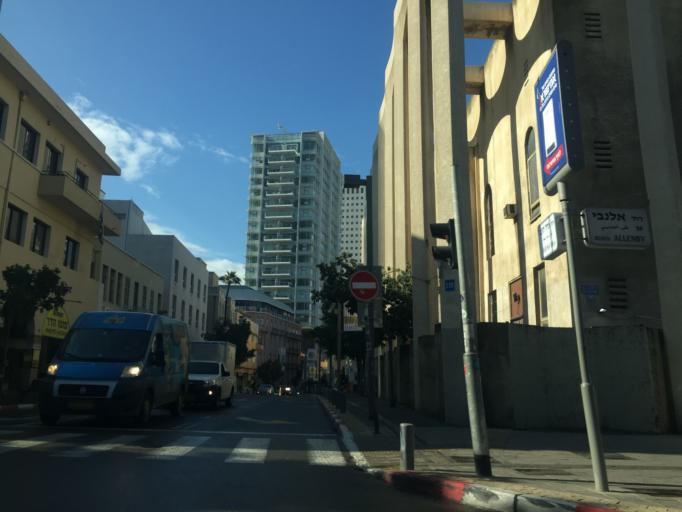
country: IL
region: Tel Aviv
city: Tel Aviv
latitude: 32.0644
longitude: 34.7727
